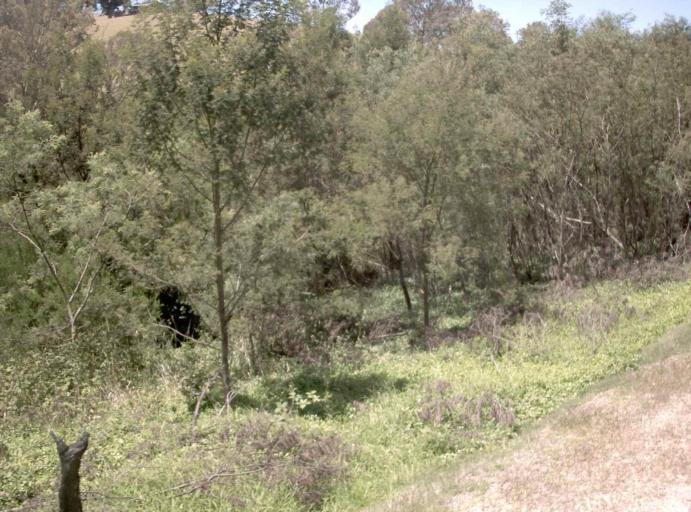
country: AU
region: Victoria
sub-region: East Gippsland
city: Bairnsdale
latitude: -37.5000
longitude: 147.8419
